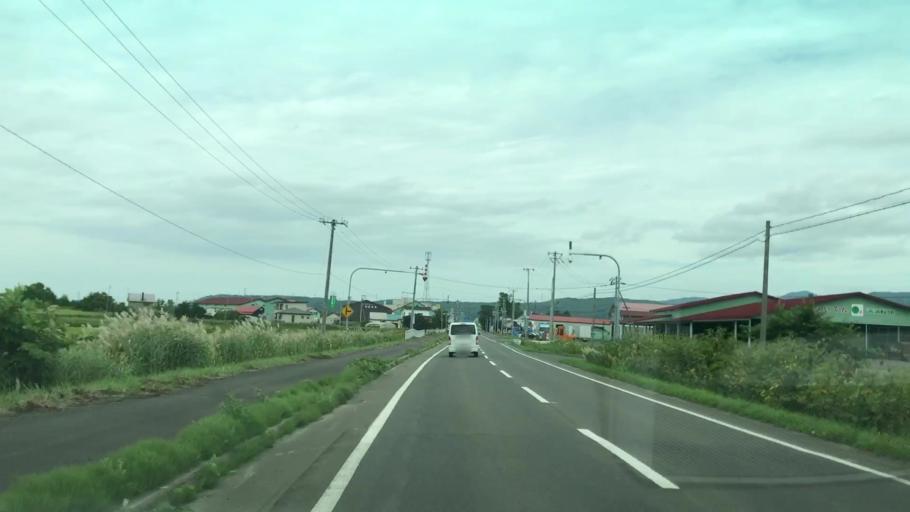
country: JP
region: Hokkaido
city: Iwanai
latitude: 43.0129
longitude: 140.5726
